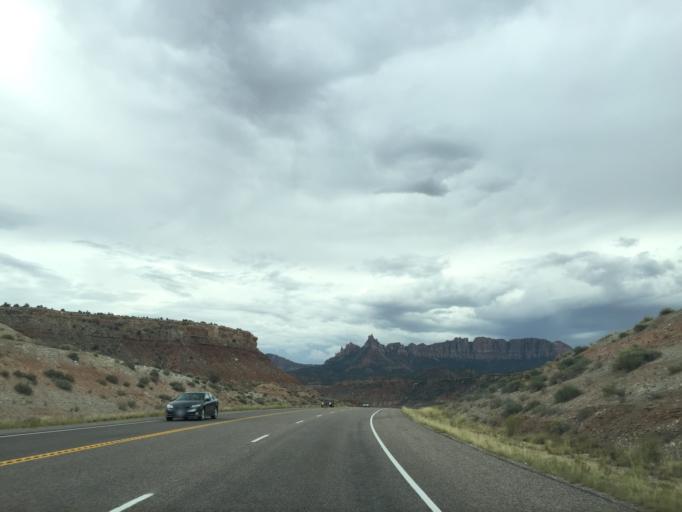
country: US
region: Utah
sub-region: Washington County
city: Hildale
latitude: 37.1698
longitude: -113.0671
